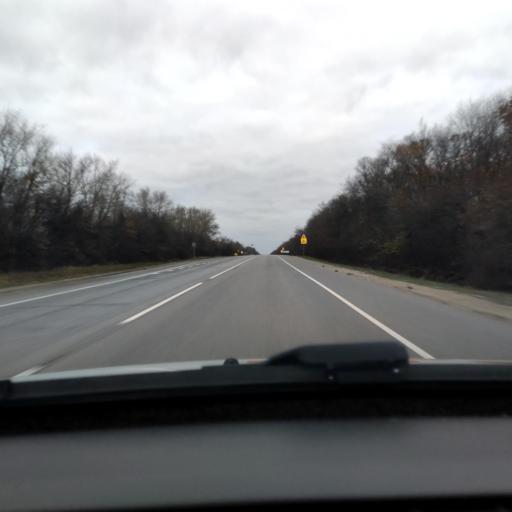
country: RU
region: Lipetsk
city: Khlevnoye
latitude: 52.3456
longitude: 39.1883
